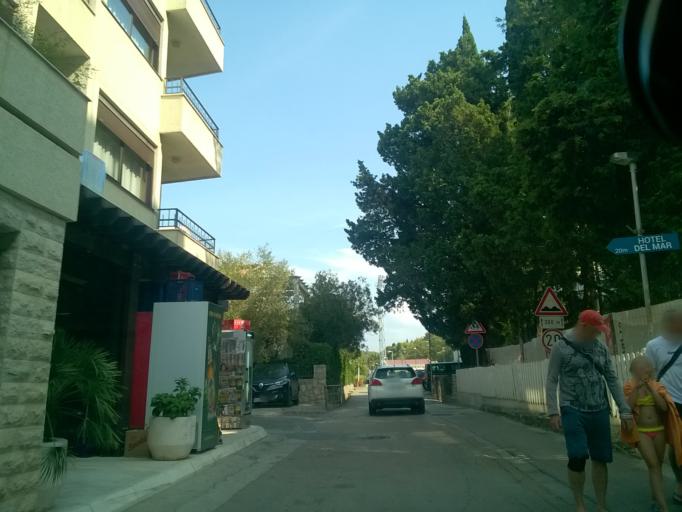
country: ME
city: Petrovac na Moru
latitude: 42.2044
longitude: 18.9452
